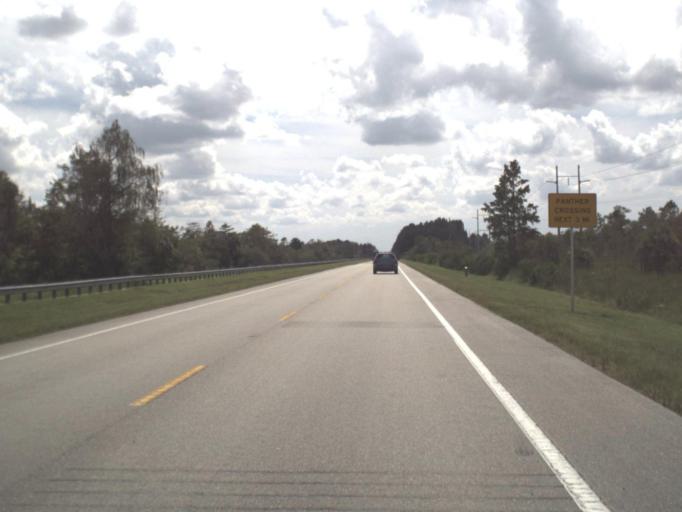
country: US
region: Florida
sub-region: Collier County
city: Lely Resort
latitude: 26.0102
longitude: -81.3463
